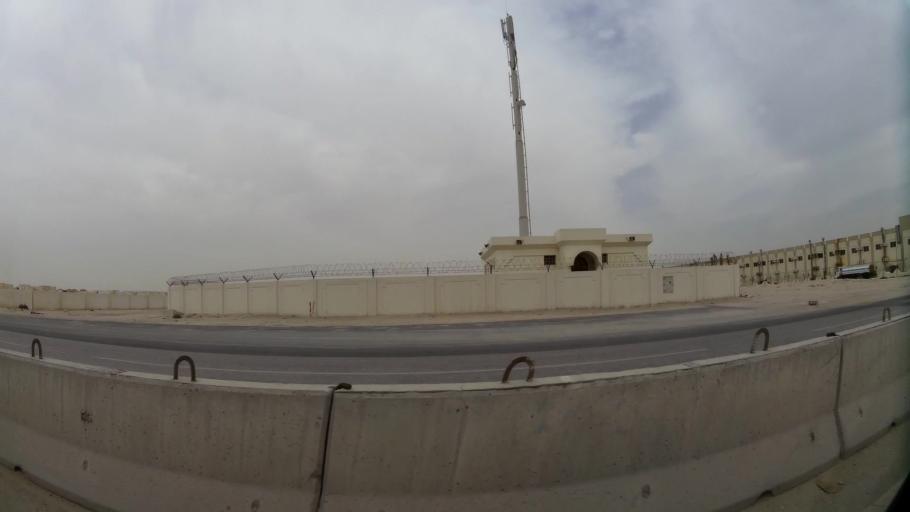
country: QA
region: Baladiyat ar Rayyan
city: Ar Rayyan
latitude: 25.2231
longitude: 51.4490
